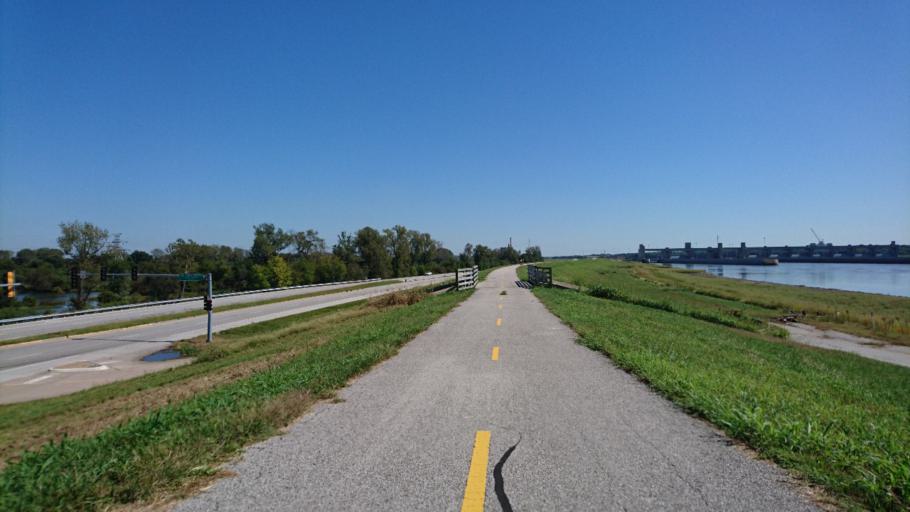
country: US
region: Illinois
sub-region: Madison County
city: Alton
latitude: 38.8783
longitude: -90.1605
